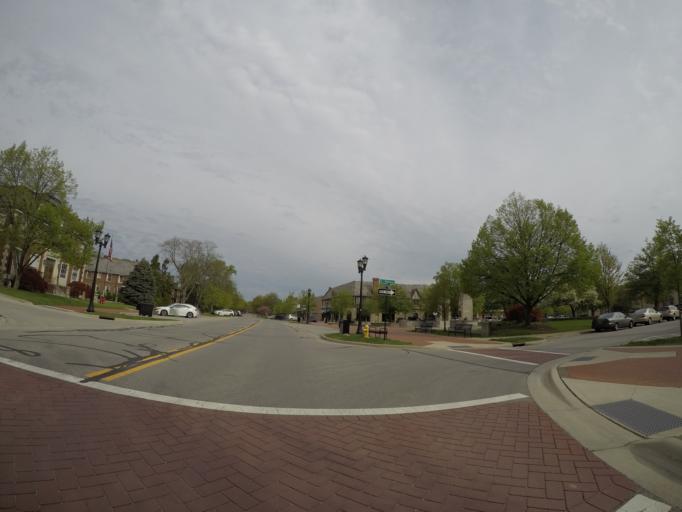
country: US
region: Ohio
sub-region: Franklin County
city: Upper Arlington
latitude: 39.9987
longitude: -83.0614
